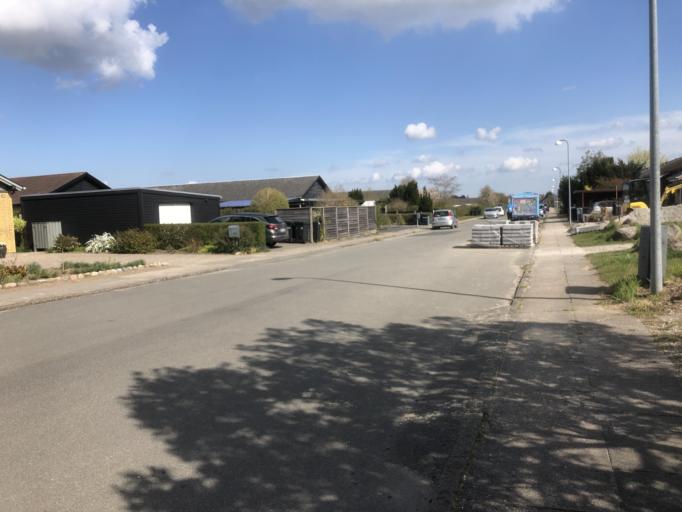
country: DK
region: South Denmark
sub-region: Odense Kommune
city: Odense
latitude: 55.4066
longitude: 10.3296
